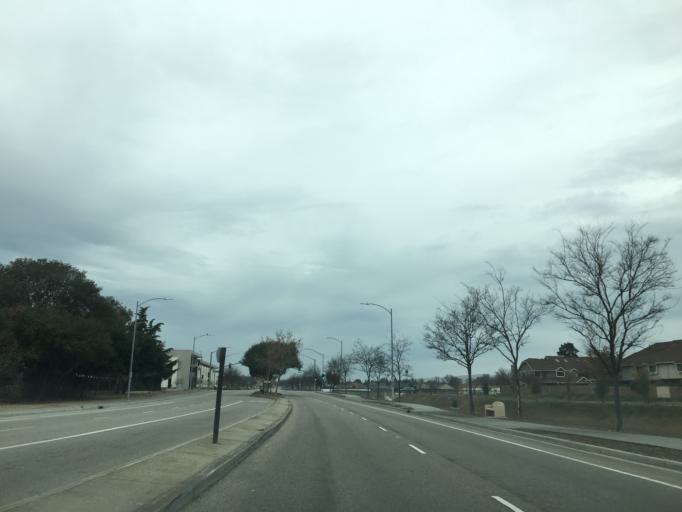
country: US
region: California
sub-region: Santa Clara County
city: Morgan Hill
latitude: 37.1275
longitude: -121.6453
